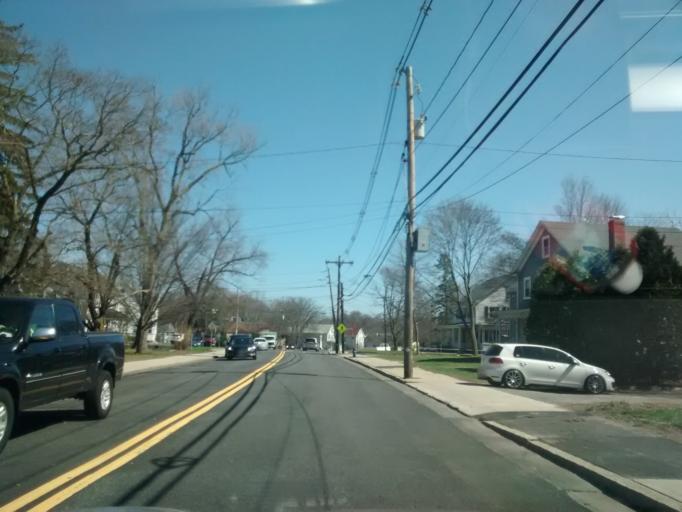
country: US
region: Massachusetts
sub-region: Middlesex County
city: Framingham Center
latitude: 42.2979
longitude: -71.4323
